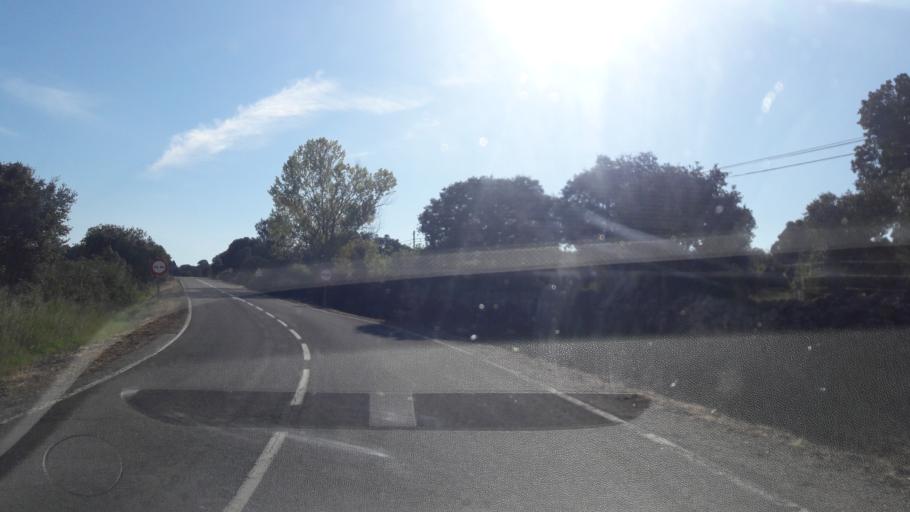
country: ES
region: Castille and Leon
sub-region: Provincia de Salamanca
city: Puente del Congosto
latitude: 40.5235
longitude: -5.4932
